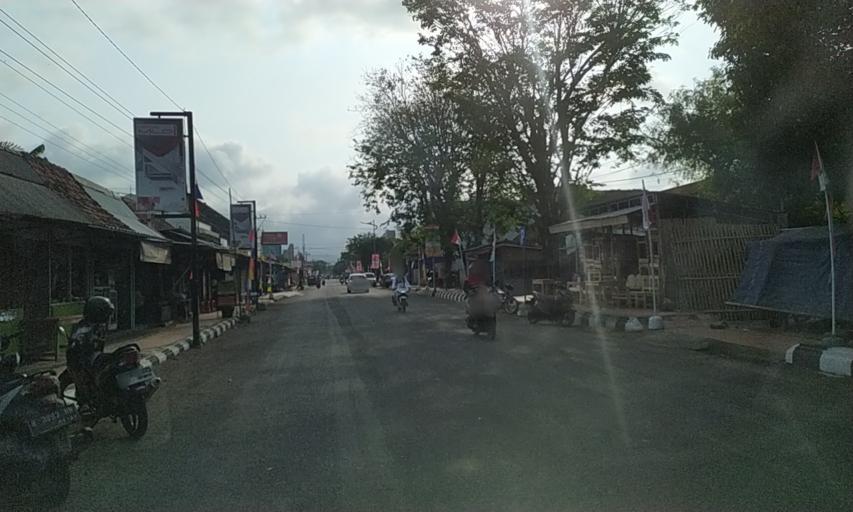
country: ID
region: Central Java
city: Karangbadar Kidul
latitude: -7.7330
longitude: 109.0060
